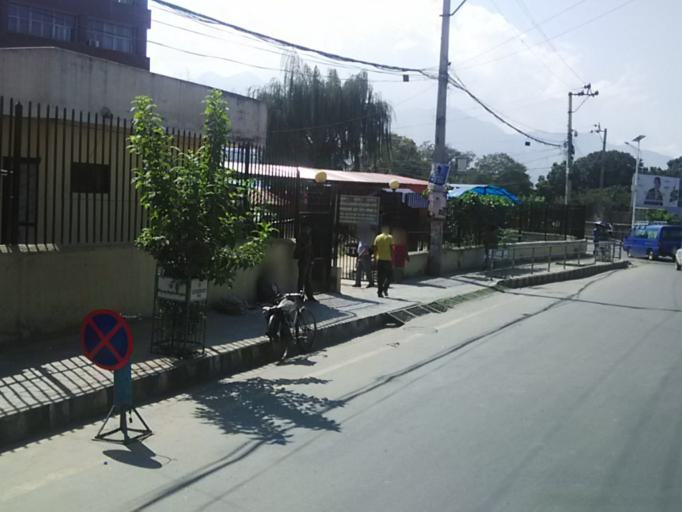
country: NP
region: Central Region
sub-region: Bagmati Zone
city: Patan
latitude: 27.6726
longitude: 85.3138
